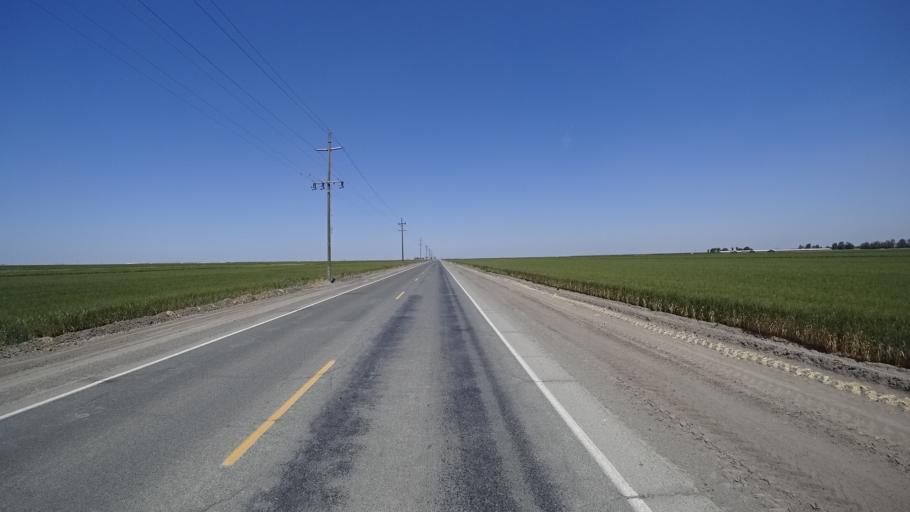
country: US
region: California
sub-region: Kings County
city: Corcoran
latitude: 36.1093
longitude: -119.6443
